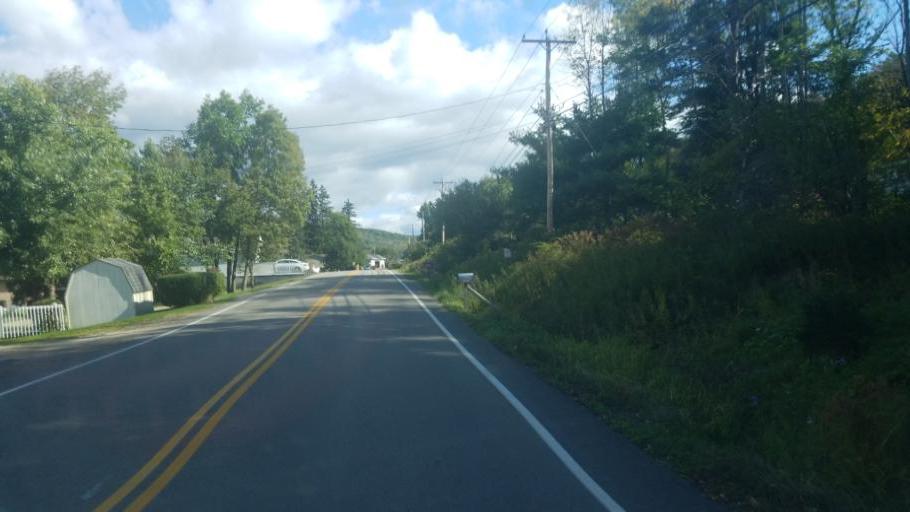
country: US
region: New York
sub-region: Allegany County
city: Cuba
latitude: 42.2452
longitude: -78.2979
